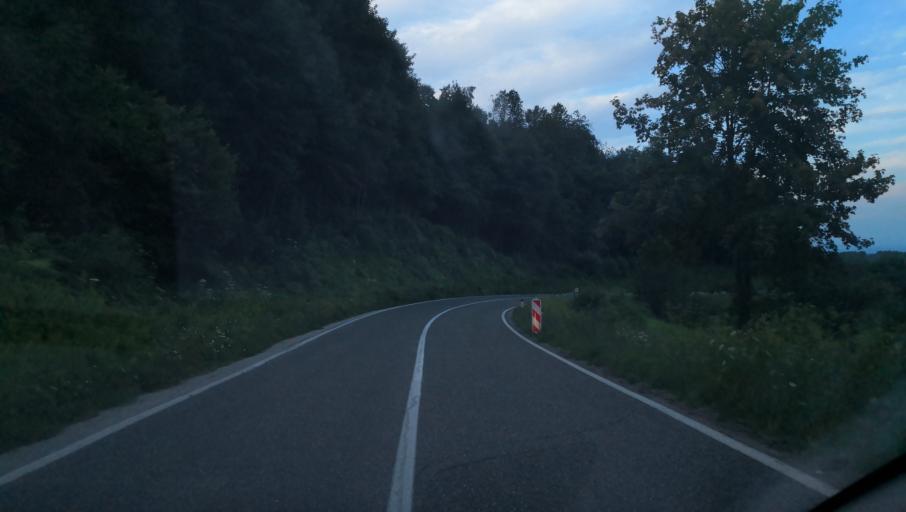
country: SI
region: Semic
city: Semic
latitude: 45.7152
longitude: 15.2318
